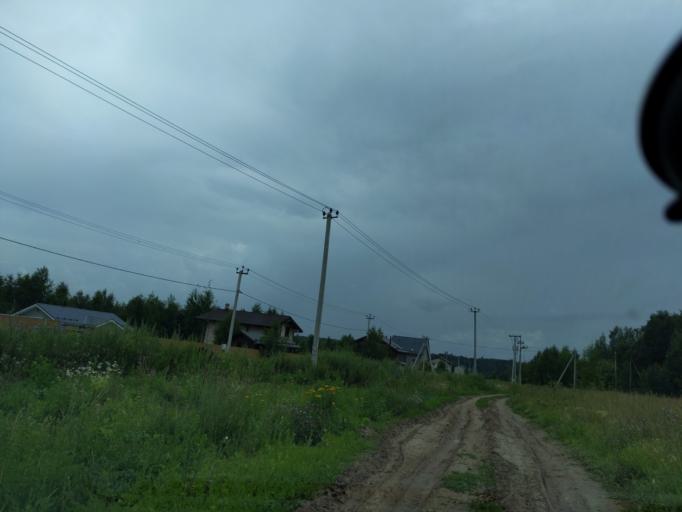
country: RU
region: Moskovskaya
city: Lugovaya
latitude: 56.0595
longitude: 37.5006
